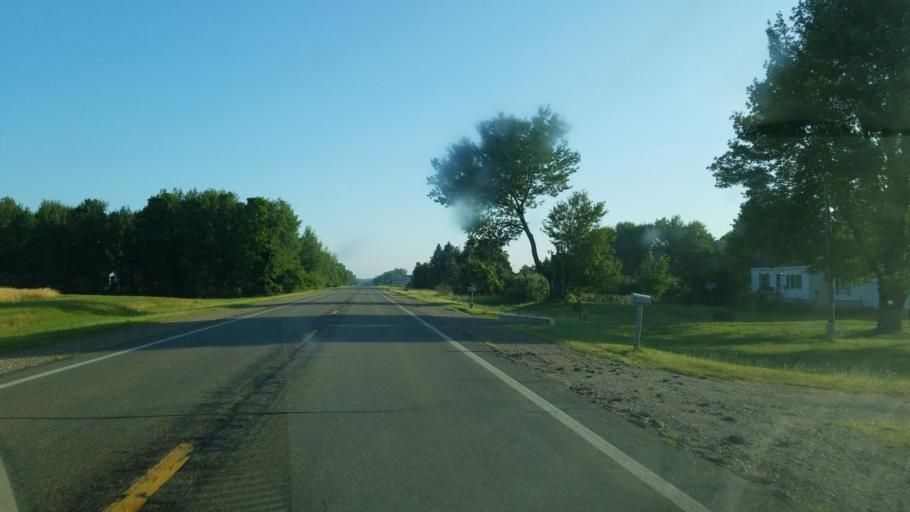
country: US
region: Michigan
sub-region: Montcalm County
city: Edmore
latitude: 43.3959
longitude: -85.0847
